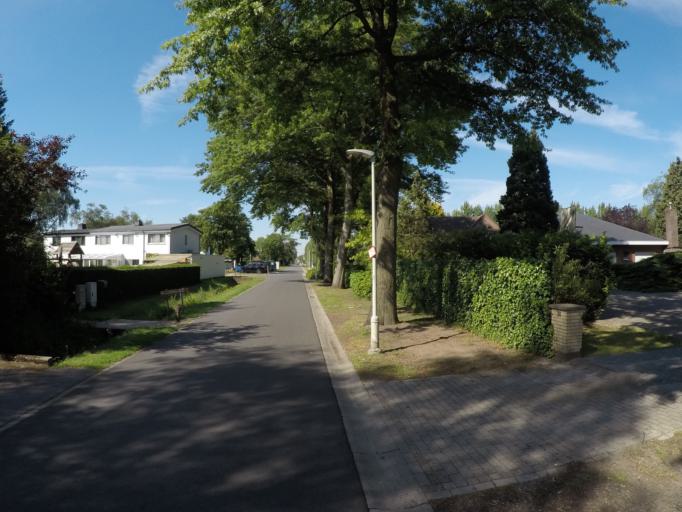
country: BE
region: Flanders
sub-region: Provincie Antwerpen
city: Kapellen
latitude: 51.3053
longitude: 4.4285
